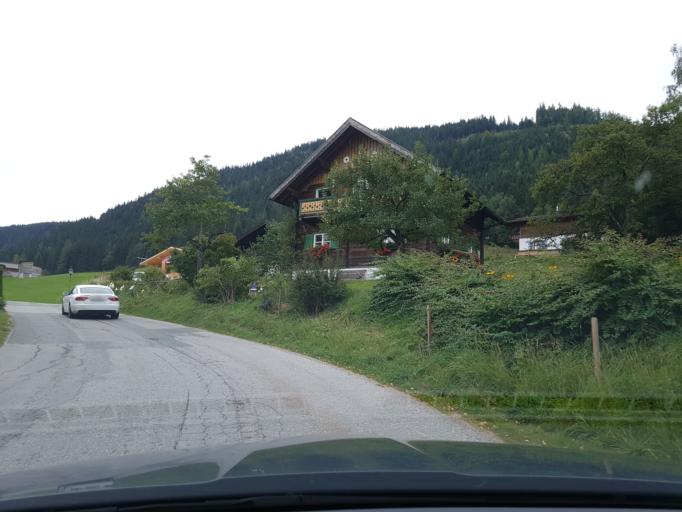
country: AT
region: Salzburg
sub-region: Politischer Bezirk Sankt Johann im Pongau
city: Forstau
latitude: 47.3751
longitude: 13.5496
